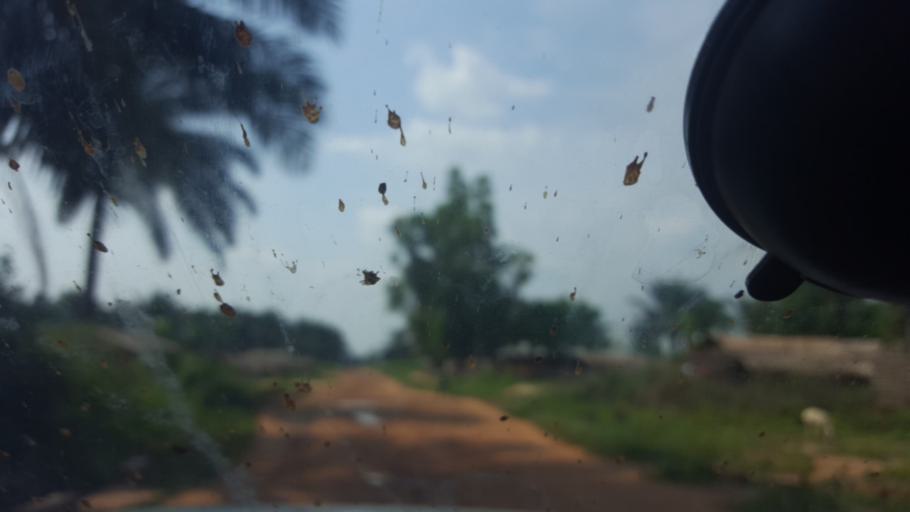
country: CD
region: Bandundu
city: Bandundu
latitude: -3.7497
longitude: 17.0382
